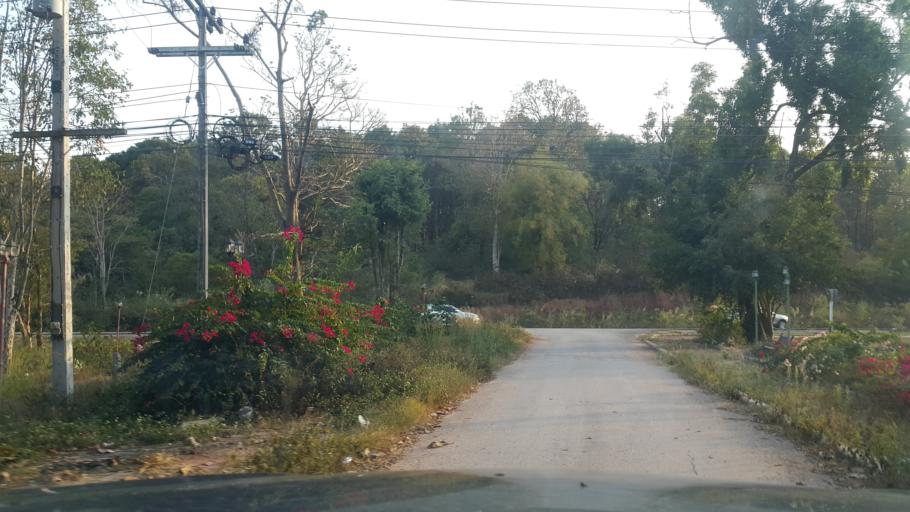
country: TH
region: Loei
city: Phu Ruea
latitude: 17.4649
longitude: 101.5168
